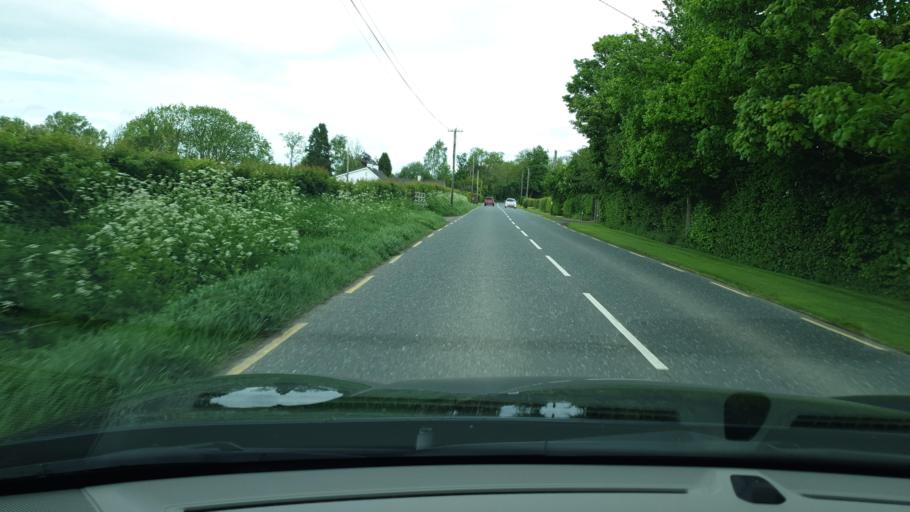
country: IE
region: Leinster
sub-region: An Mhi
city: Ratoath
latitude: 53.5316
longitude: -6.4501
